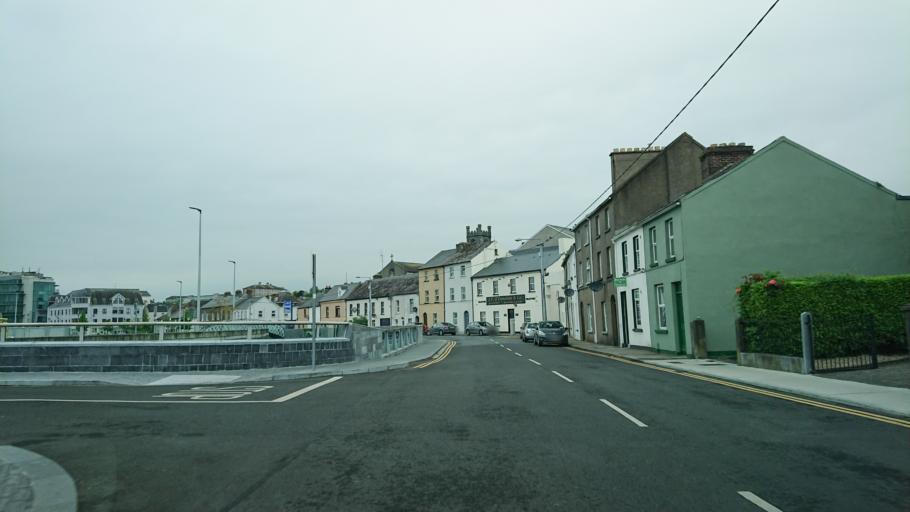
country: IE
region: Munster
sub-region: Waterford
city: Waterford
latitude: 52.2571
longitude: -7.1078
